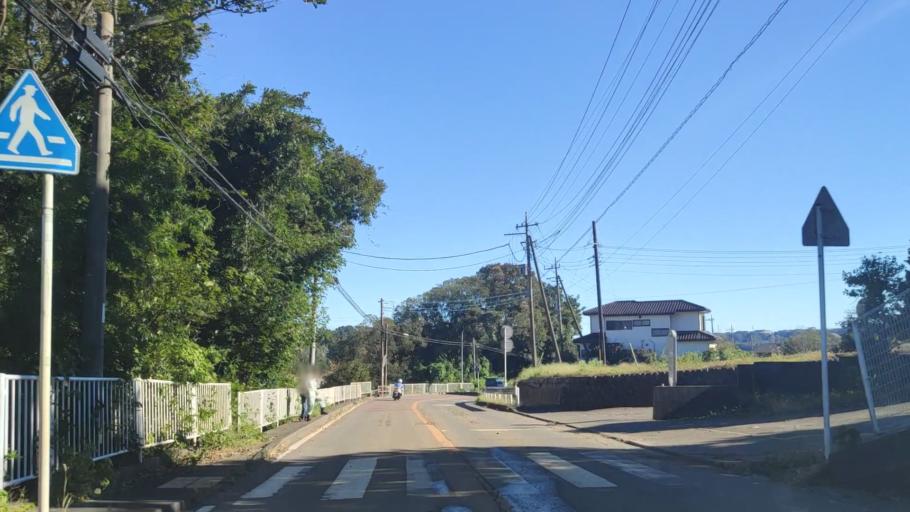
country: JP
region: Tokyo
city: Hachioji
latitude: 35.5609
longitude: 139.3181
